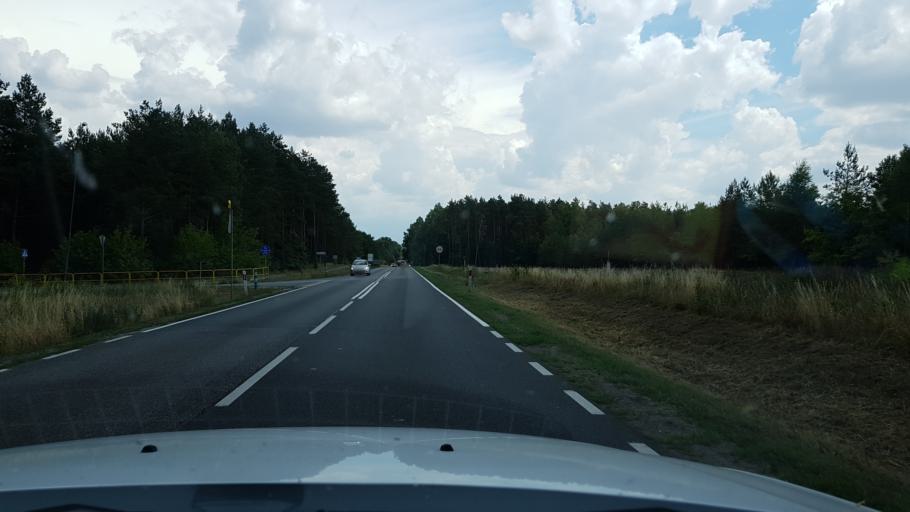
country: PL
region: West Pomeranian Voivodeship
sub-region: Powiat walecki
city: Walcz
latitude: 53.2933
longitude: 16.4284
